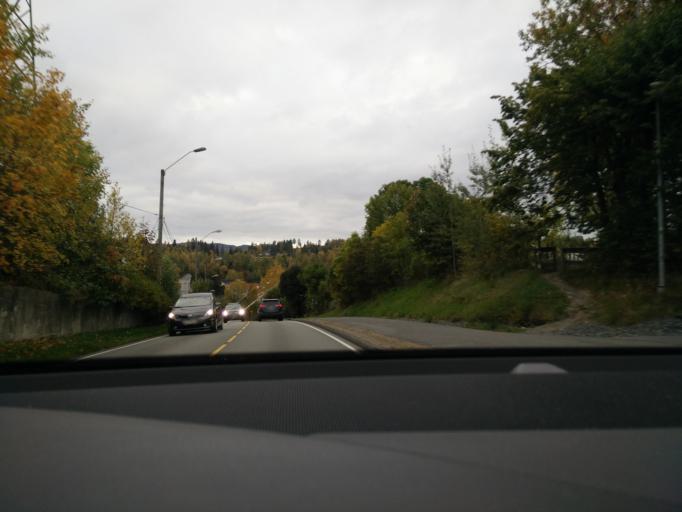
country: NO
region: Akershus
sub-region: Baerum
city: Lysaker
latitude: 59.9340
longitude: 10.6124
